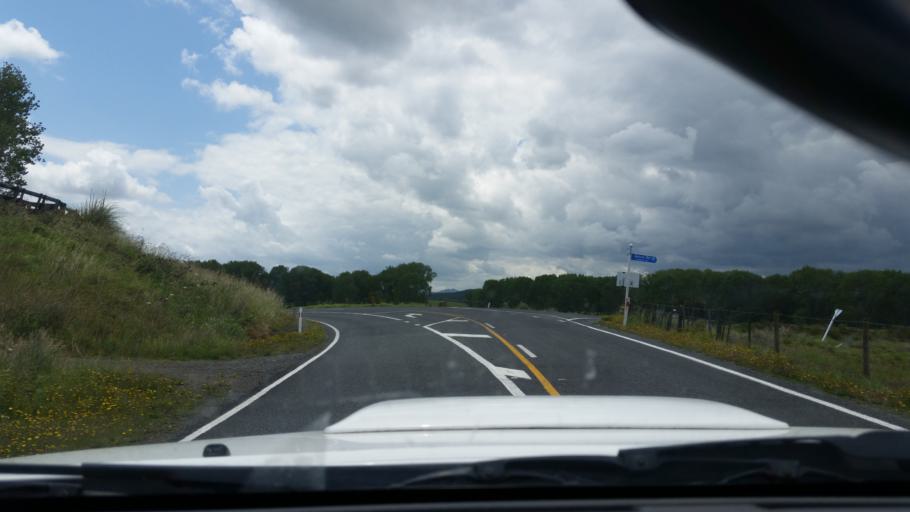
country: NZ
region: Northland
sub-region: Kaipara District
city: Dargaville
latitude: -35.8557
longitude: 173.8484
